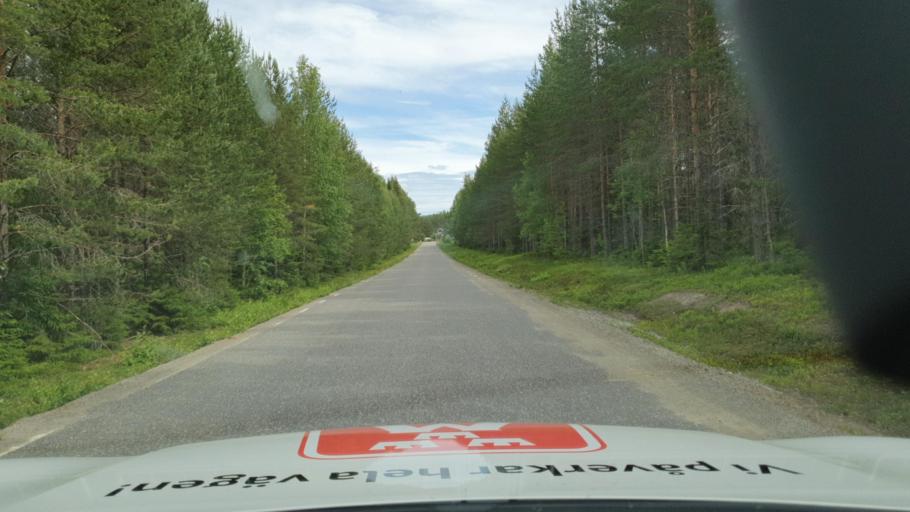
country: SE
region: Vaesterbotten
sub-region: Skelleftea Kommun
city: Viken
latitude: 64.4976
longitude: 20.8981
